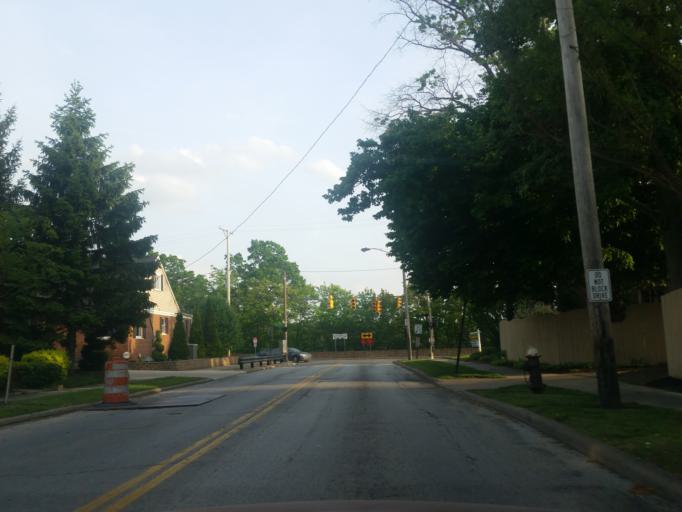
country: US
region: Ohio
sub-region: Cuyahoga County
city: Lakewood
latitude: 41.4685
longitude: -81.8163
